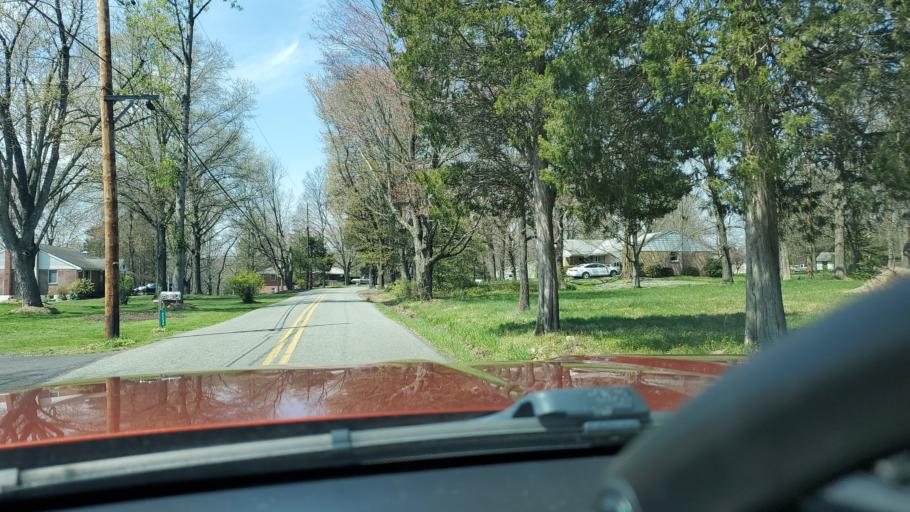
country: US
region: Pennsylvania
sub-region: Montgomery County
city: Gilbertsville
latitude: 40.3299
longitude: -75.5430
